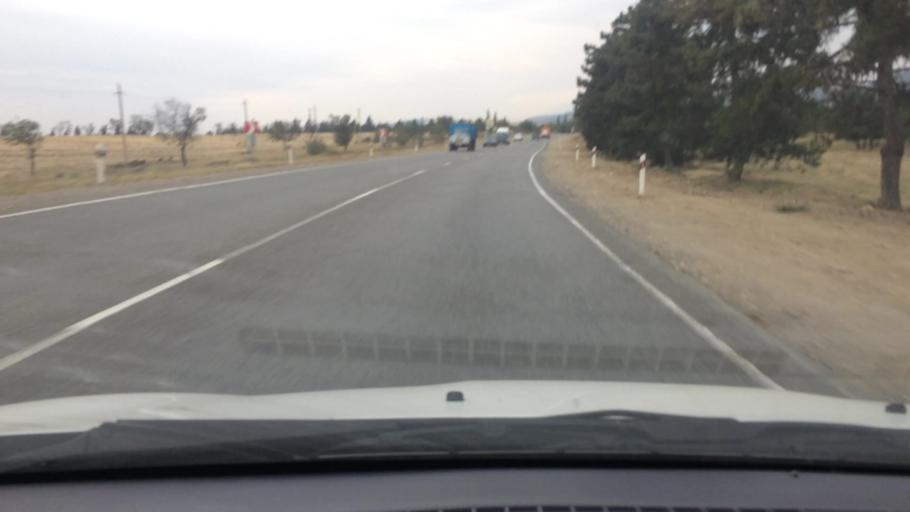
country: GE
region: T'bilisi
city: Tbilisi
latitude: 41.6385
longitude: 44.8749
